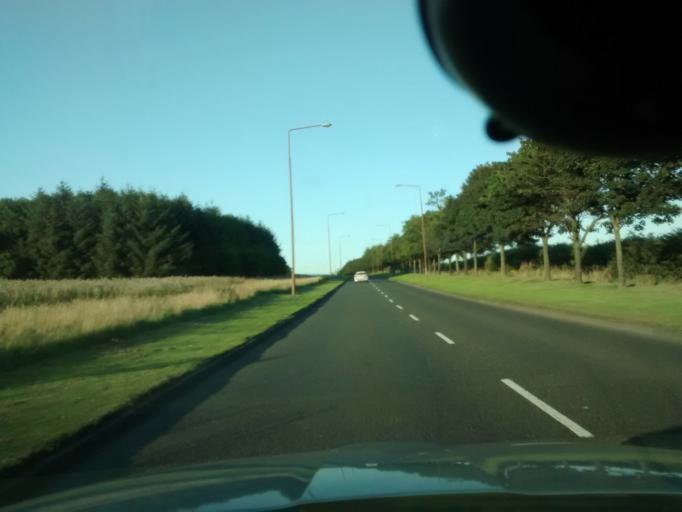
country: GB
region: Scotland
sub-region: West Lothian
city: West Calder
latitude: 55.8988
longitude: -3.5906
